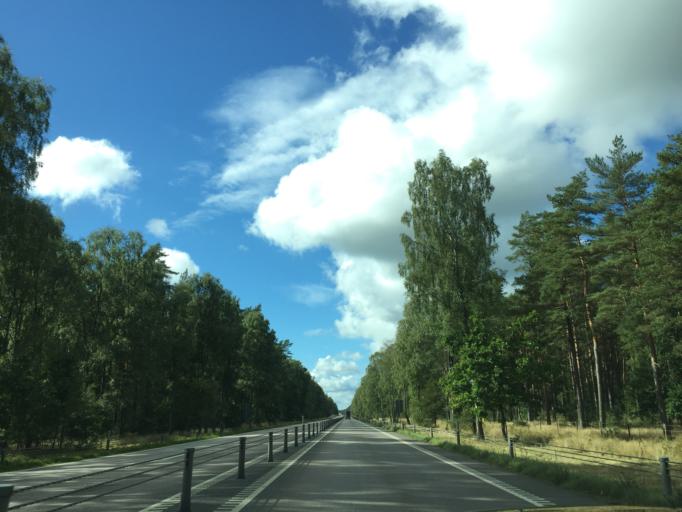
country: SE
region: Skane
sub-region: Sjobo Kommun
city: Sjoebo
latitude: 55.6381
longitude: 13.6454
